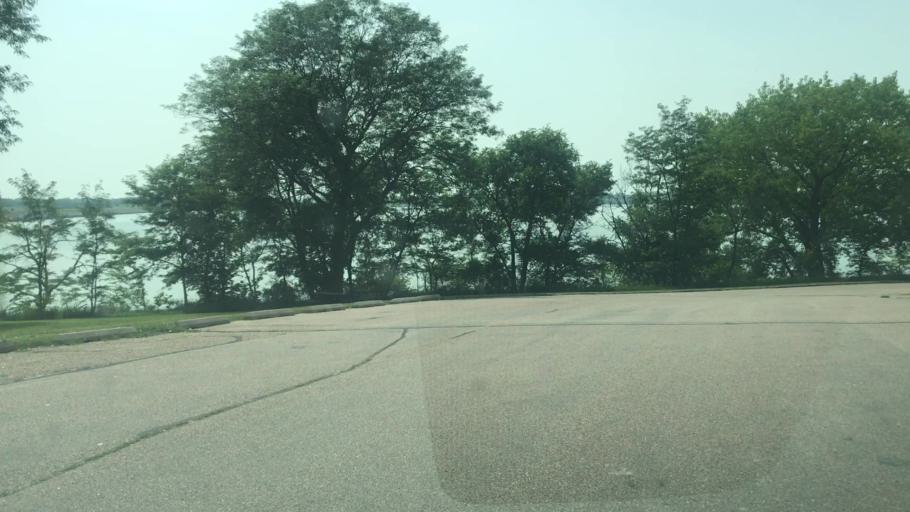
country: US
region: Nebraska
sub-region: Sherman County
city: Loup City
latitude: 41.3084
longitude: -98.8757
